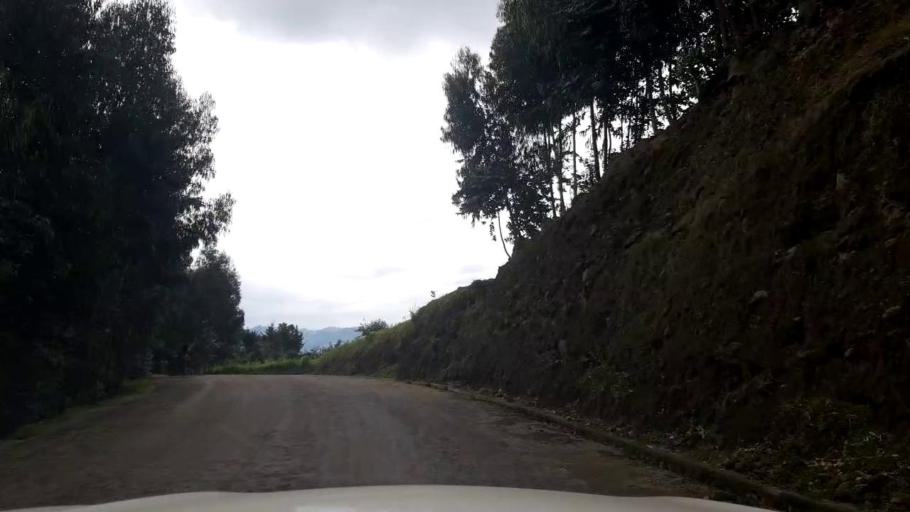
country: RW
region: Northern Province
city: Musanze
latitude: -1.5252
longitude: 29.5308
